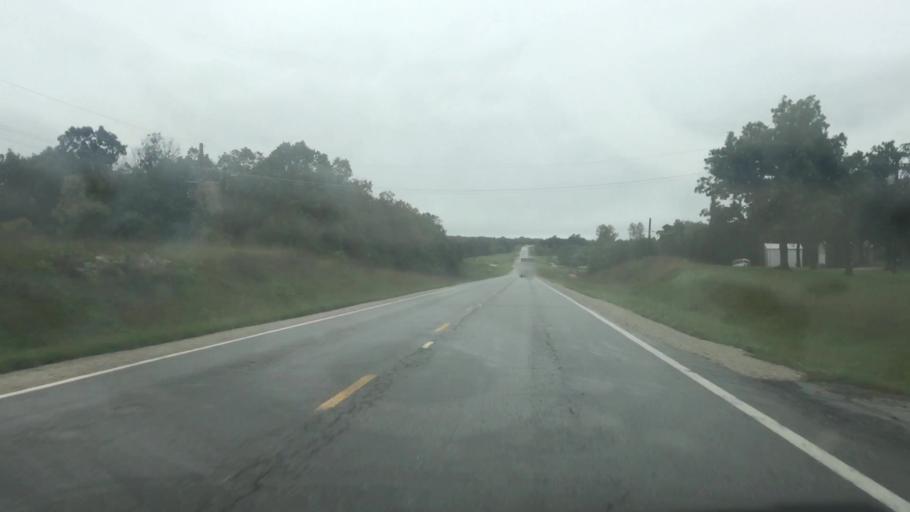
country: US
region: Kansas
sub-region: Anderson County
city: Garnett
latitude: 38.2171
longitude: -95.2487
